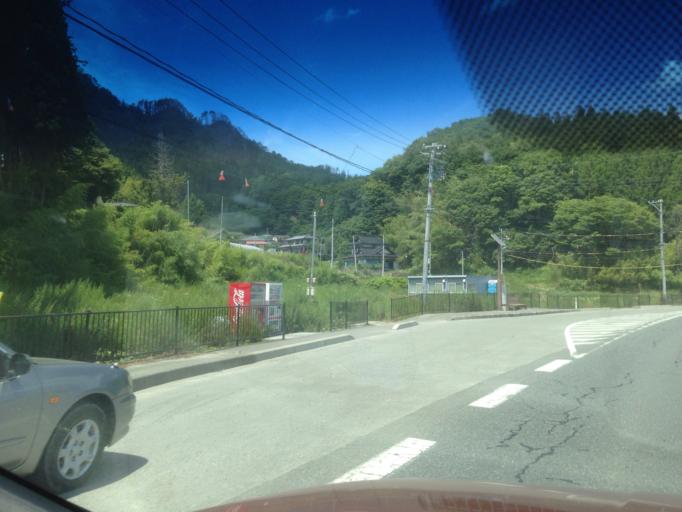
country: JP
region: Iwate
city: Otsuchi
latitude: 39.3363
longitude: 141.8907
